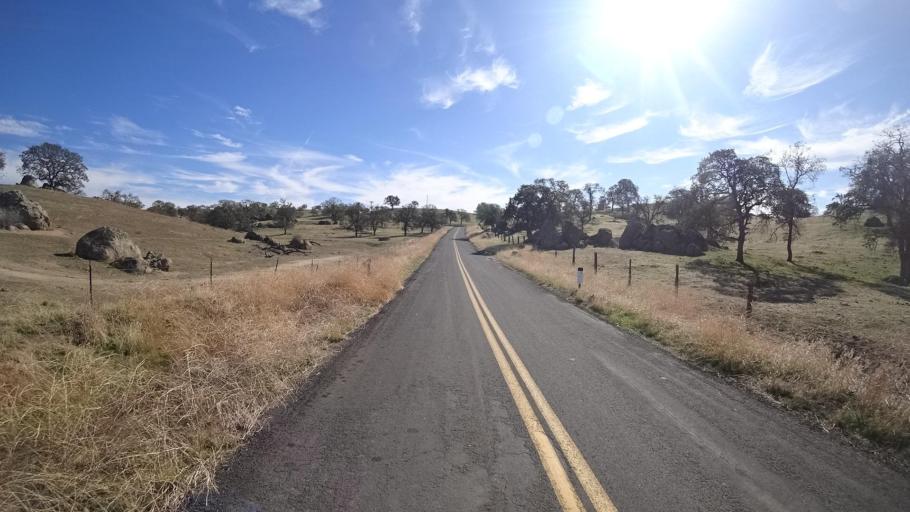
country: US
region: California
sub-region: Kern County
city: Oildale
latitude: 35.6218
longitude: -118.8496
